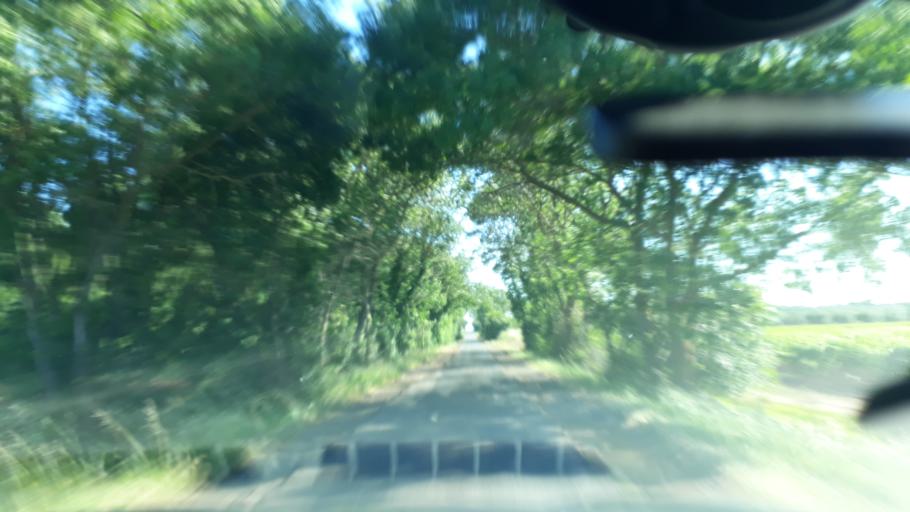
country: FR
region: Languedoc-Roussillon
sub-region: Departement de l'Herault
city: Marseillan
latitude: 43.3372
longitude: 3.5065
